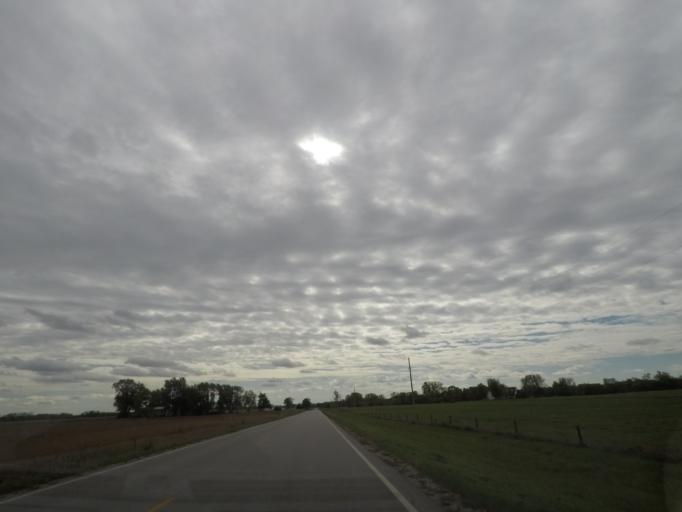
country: US
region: Iowa
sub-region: Story County
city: Huxley
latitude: 41.8491
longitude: -93.5316
